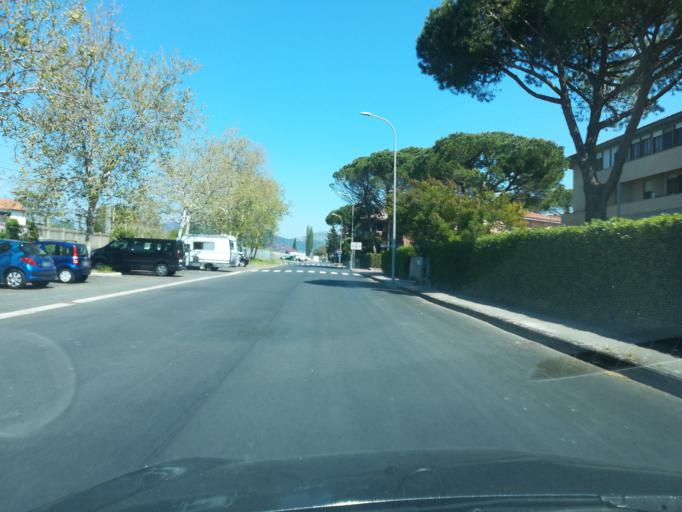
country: IT
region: Tuscany
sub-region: Province of Pisa
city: Pisa
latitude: 43.7308
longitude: 10.3971
